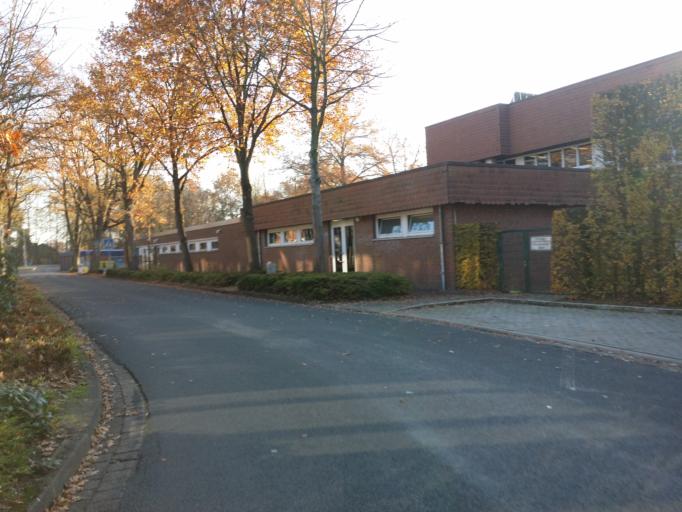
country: DE
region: Lower Saxony
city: Rotenburg
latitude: 53.0968
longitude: 9.3744
